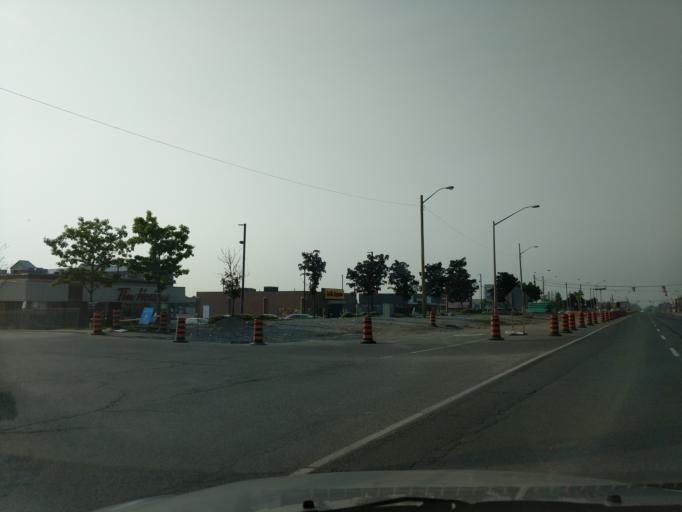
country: CA
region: Ontario
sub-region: York
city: Richmond Hill
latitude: 43.8964
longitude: -79.4431
